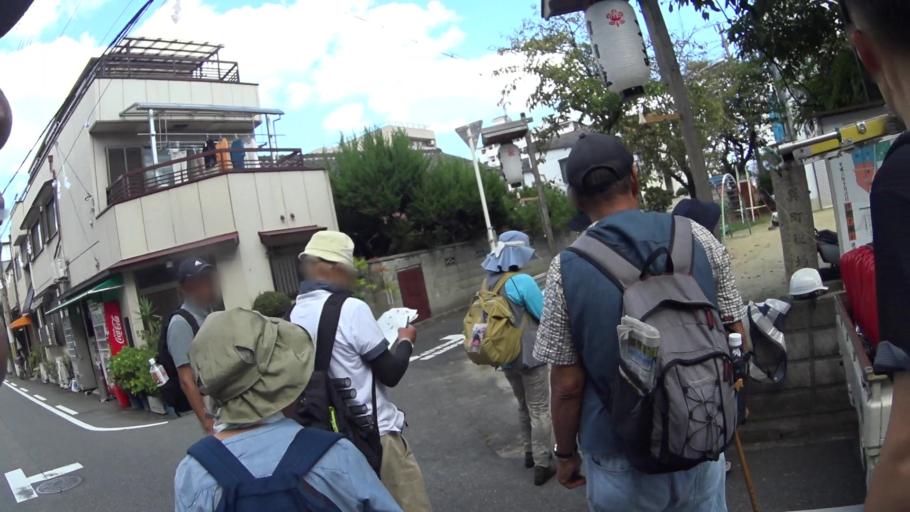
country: JP
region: Osaka
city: Yao
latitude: 34.6457
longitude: 135.5523
